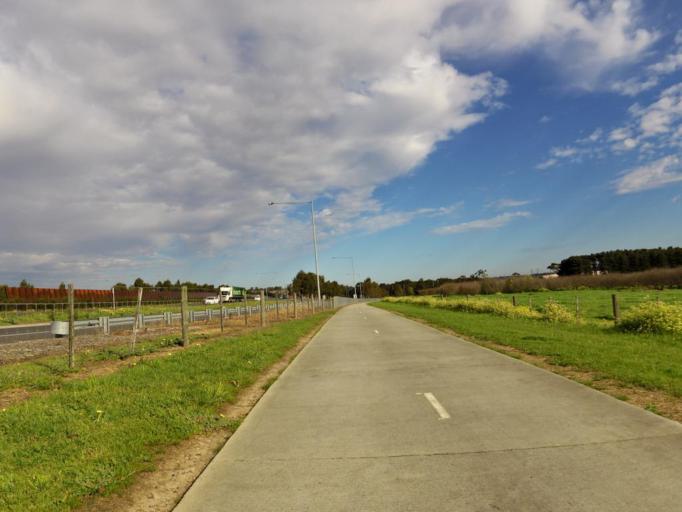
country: AU
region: Victoria
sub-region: Knox
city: Wantirna South
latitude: -37.8733
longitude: 145.2113
